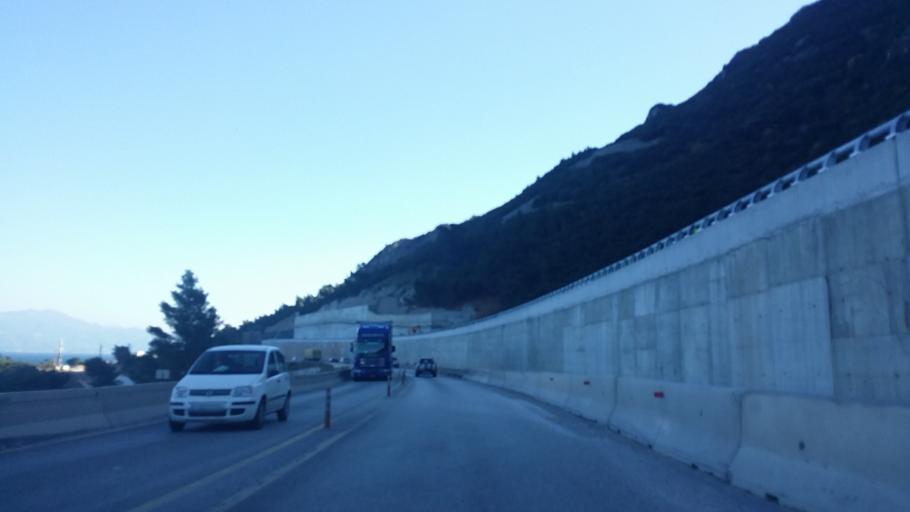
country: GR
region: West Greece
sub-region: Nomos Achaias
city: Ano Kastritsion
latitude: 38.3231
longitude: 21.9042
